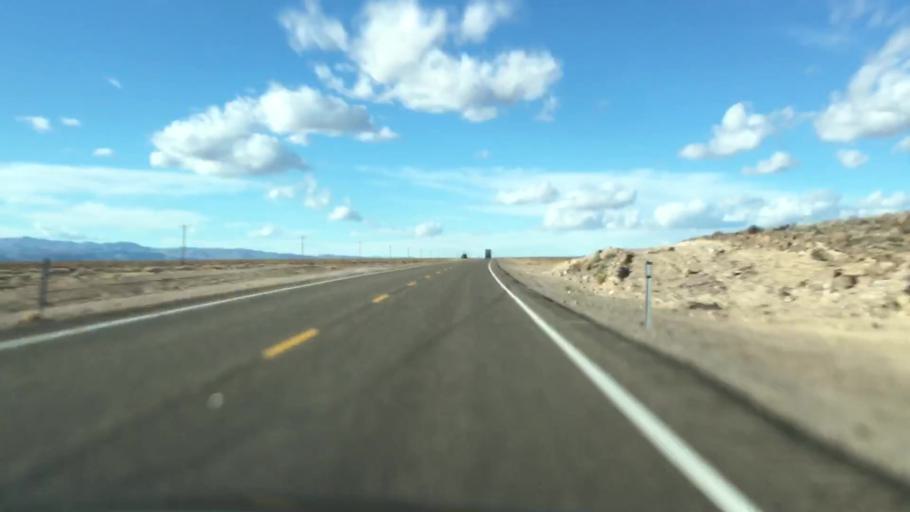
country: US
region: Nevada
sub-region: Nye County
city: Beatty
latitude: 37.1925
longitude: -116.9455
